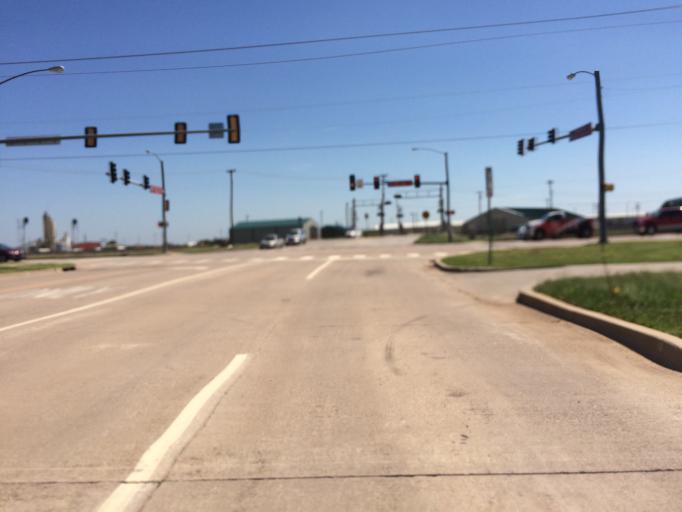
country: US
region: Oklahoma
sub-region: Cleveland County
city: Norman
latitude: 35.2468
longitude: -97.4614
